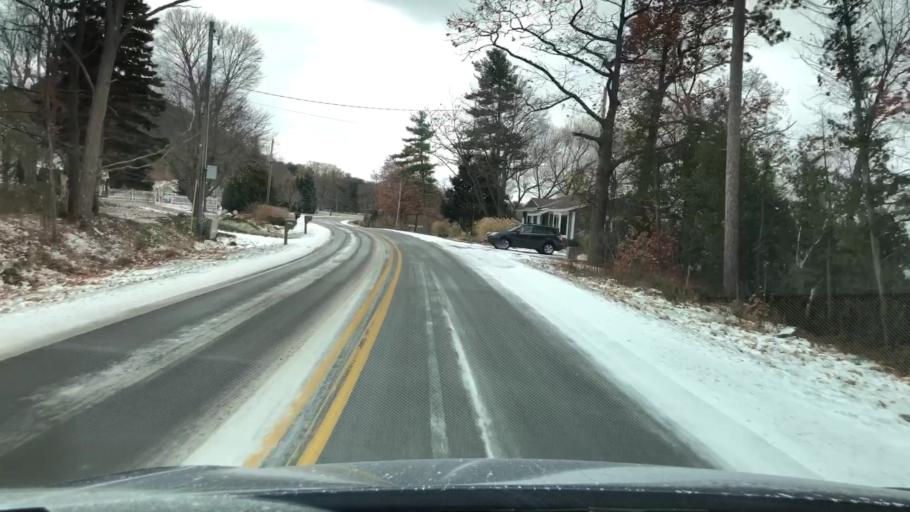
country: US
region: Michigan
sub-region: Leelanau County
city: Greilickville
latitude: 44.8528
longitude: -85.5543
